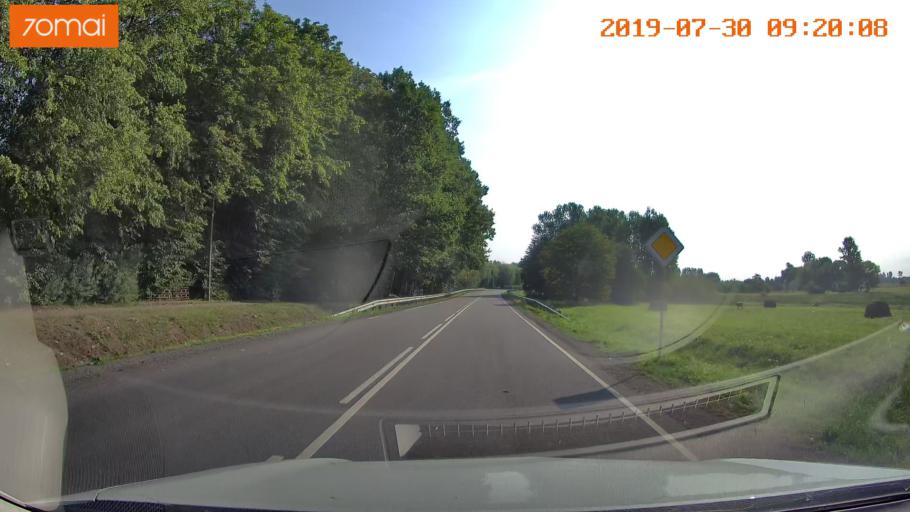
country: RU
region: Kaliningrad
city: Nesterov
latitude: 54.6353
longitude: 22.6047
